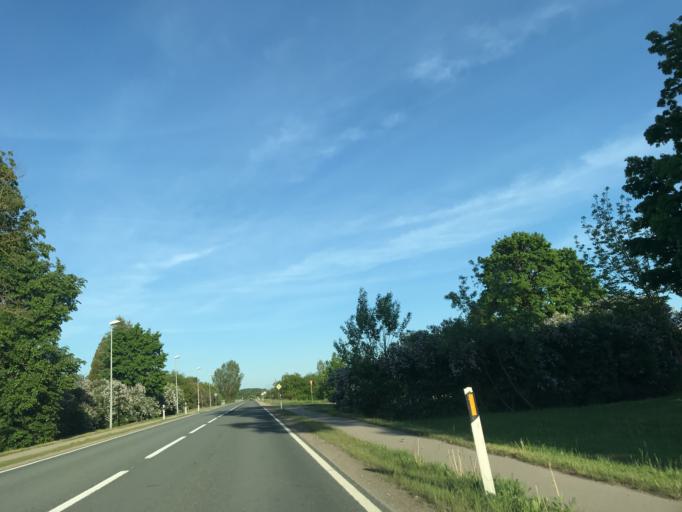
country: LV
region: Olaine
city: Olaine
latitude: 56.6271
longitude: 23.9410
